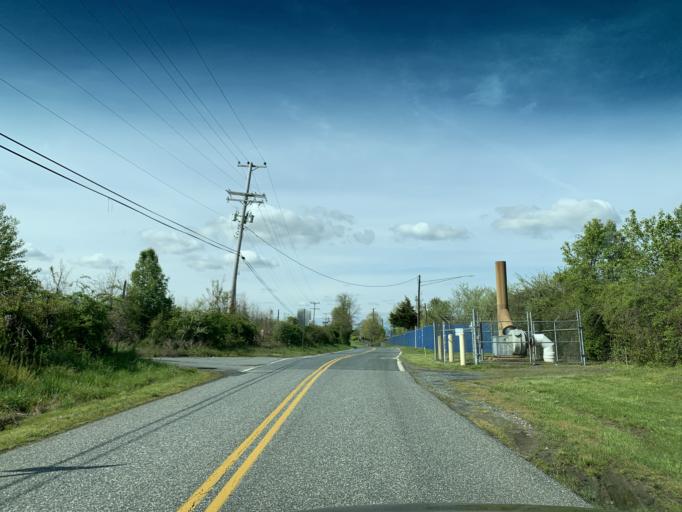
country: US
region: Maryland
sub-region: Harford County
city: Perryman
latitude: 39.4373
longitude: -76.2161
